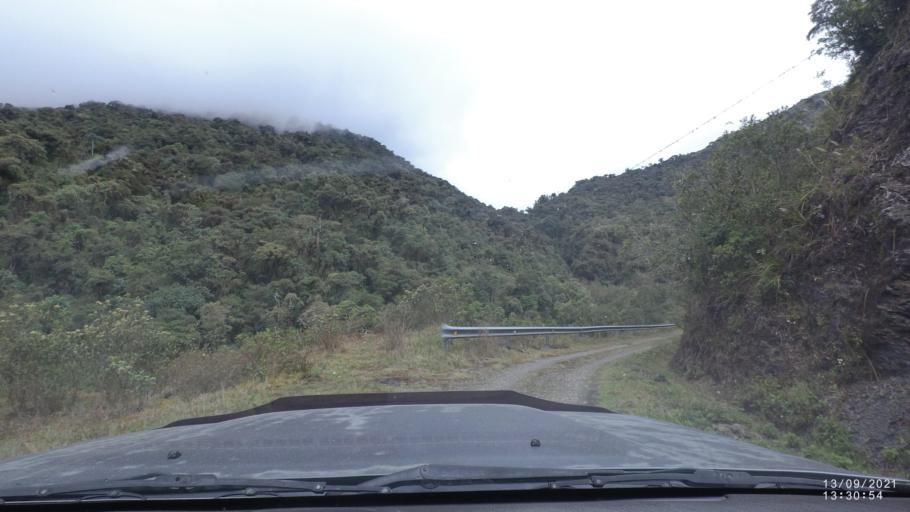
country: BO
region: Cochabamba
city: Colomi
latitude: -17.2189
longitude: -65.8603
